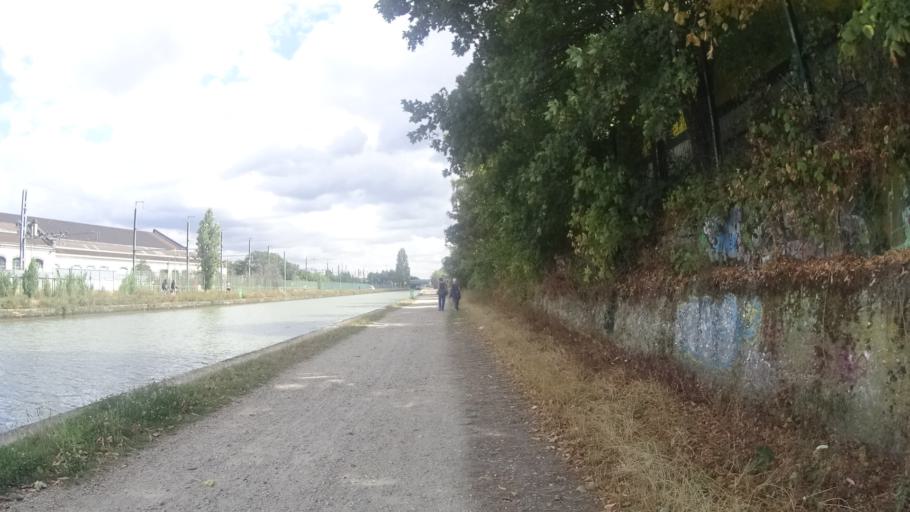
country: FR
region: Ile-de-France
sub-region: Departement de Seine-Saint-Denis
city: Romainville
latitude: 48.8970
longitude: 2.4301
